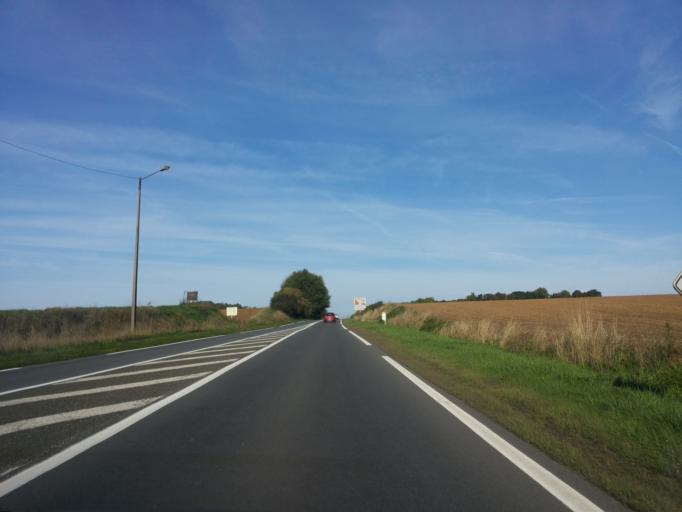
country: FR
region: Picardie
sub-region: Departement de l'Aisne
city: Charmes
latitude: 49.6323
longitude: 3.4196
